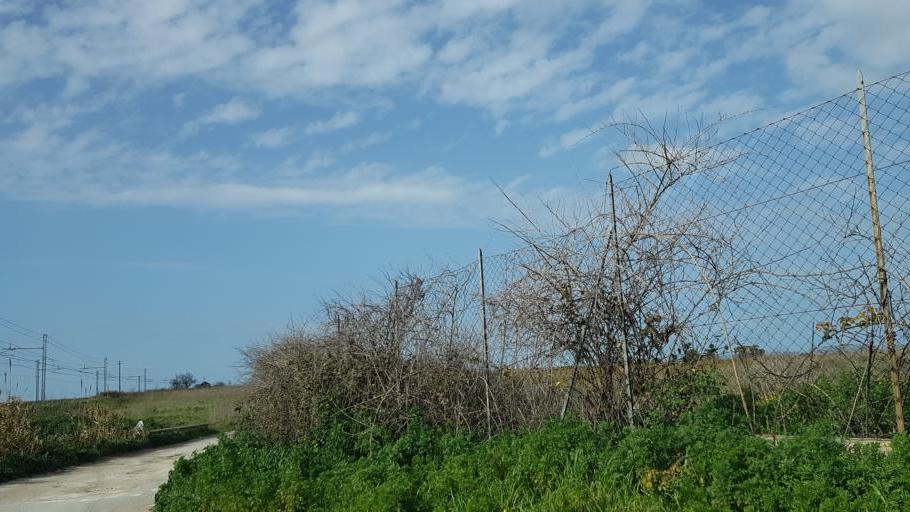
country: IT
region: Apulia
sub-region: Provincia di Brindisi
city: Brindisi
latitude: 40.6234
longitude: 17.9025
